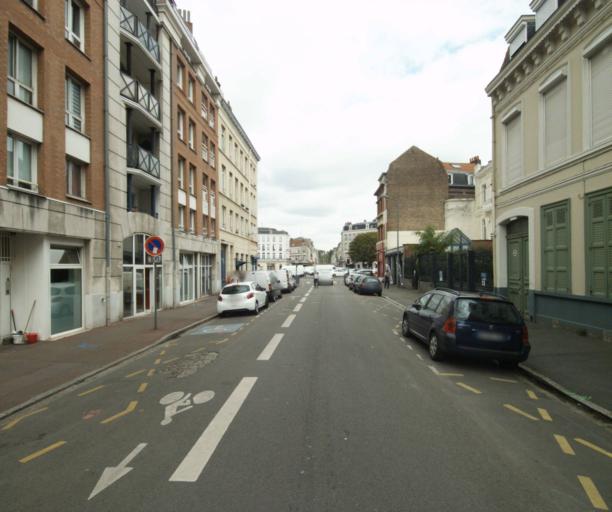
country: FR
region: Nord-Pas-de-Calais
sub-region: Departement du Nord
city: Lille
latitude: 50.6314
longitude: 3.0532
